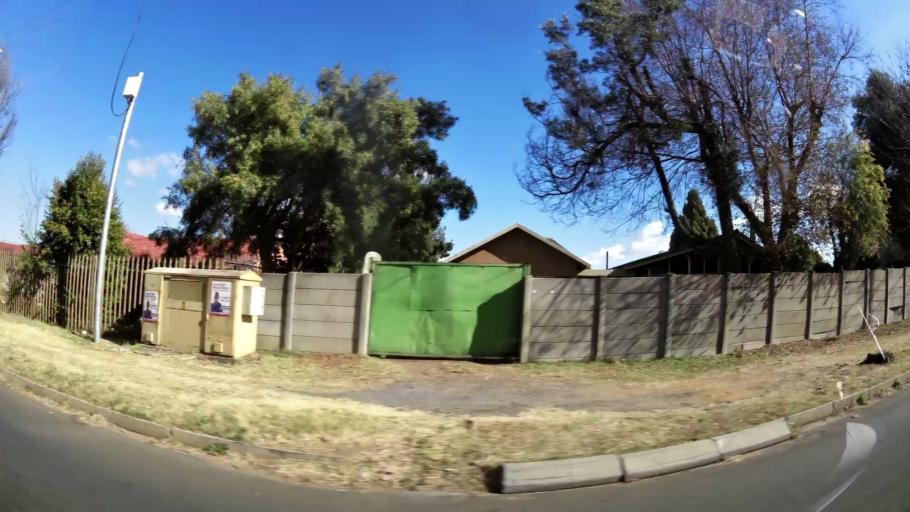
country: ZA
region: Gauteng
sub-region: City of Johannesburg Metropolitan Municipality
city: Roodepoort
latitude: -26.1411
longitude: 27.8356
